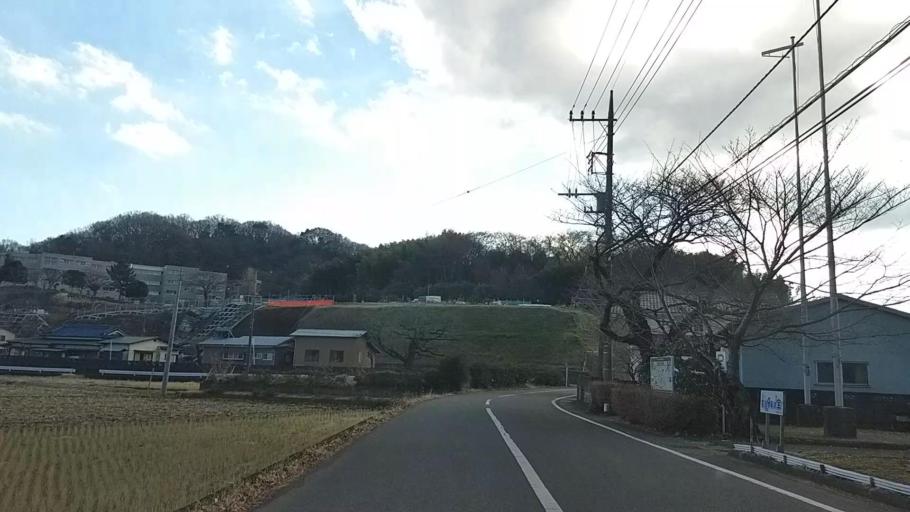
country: JP
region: Kanagawa
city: Atsugi
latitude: 35.4325
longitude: 139.3194
